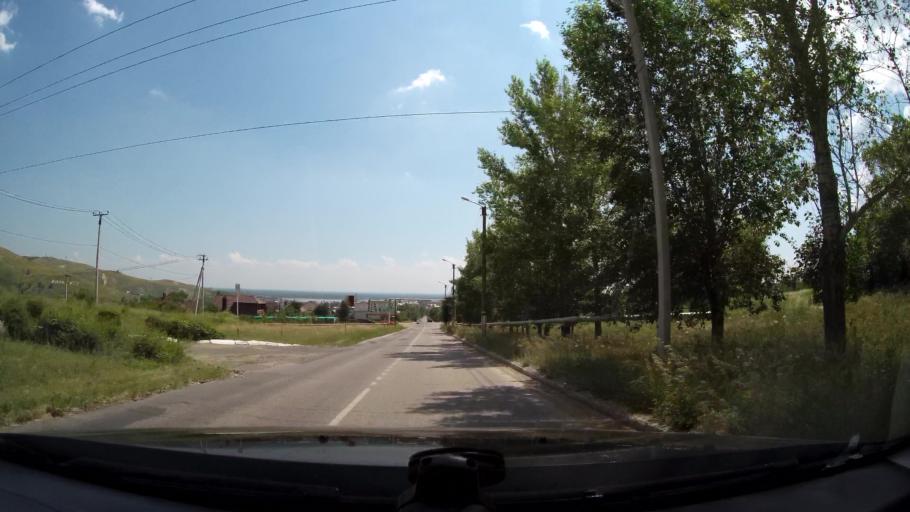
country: RU
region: Saratov
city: Vol'sk
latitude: 52.0657
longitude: 47.3771
